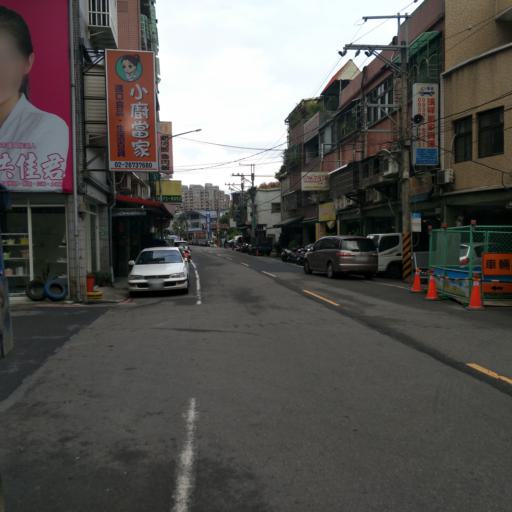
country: TW
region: Taiwan
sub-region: Taoyuan
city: Taoyuan
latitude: 24.9377
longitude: 121.3748
